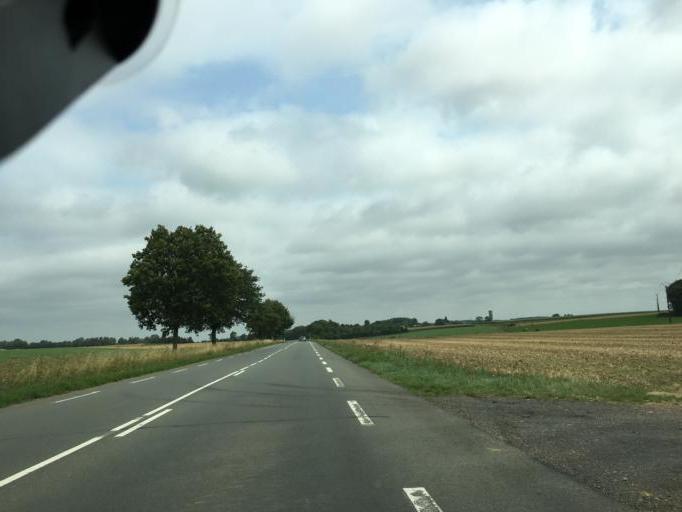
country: FR
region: Nord-Pas-de-Calais
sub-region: Departement du Pas-de-Calais
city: Camblain-Chatelain
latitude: 50.4261
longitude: 2.4338
